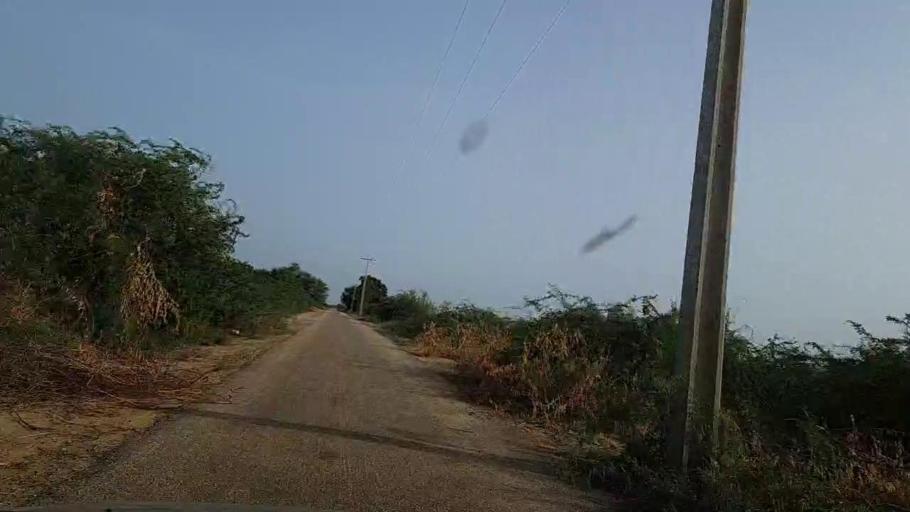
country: PK
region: Sindh
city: Kotri
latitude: 25.1985
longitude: 68.2577
